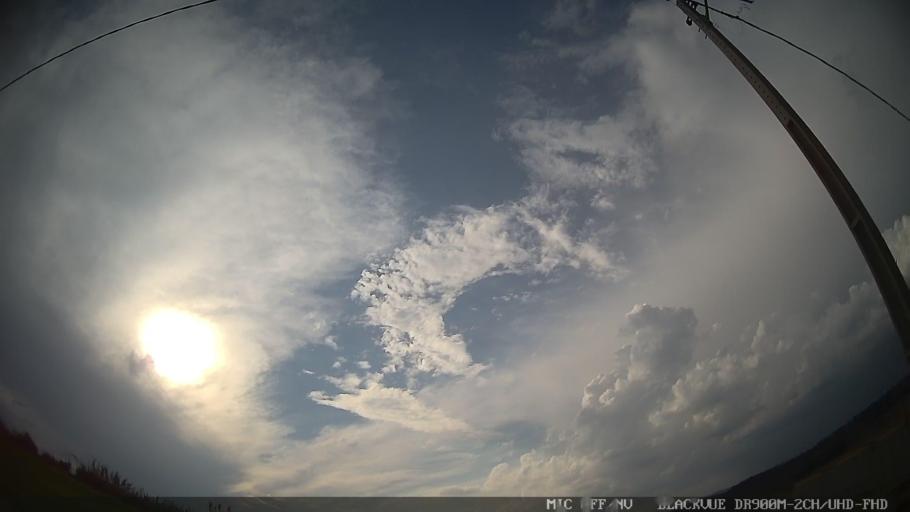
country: BR
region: Sao Paulo
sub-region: Braganca Paulista
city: Braganca Paulista
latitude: -22.9088
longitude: -46.5587
